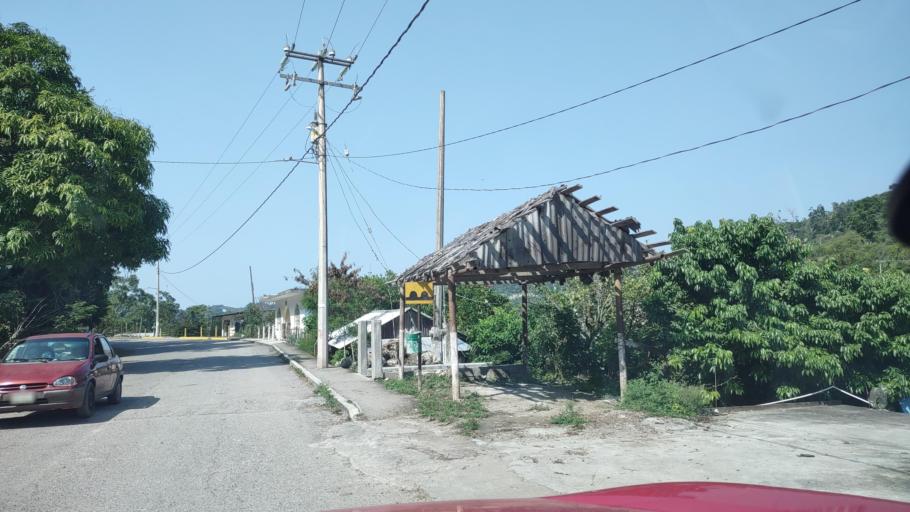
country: MX
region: Veracruz
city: Agua Dulce
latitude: 20.3163
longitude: -97.1727
